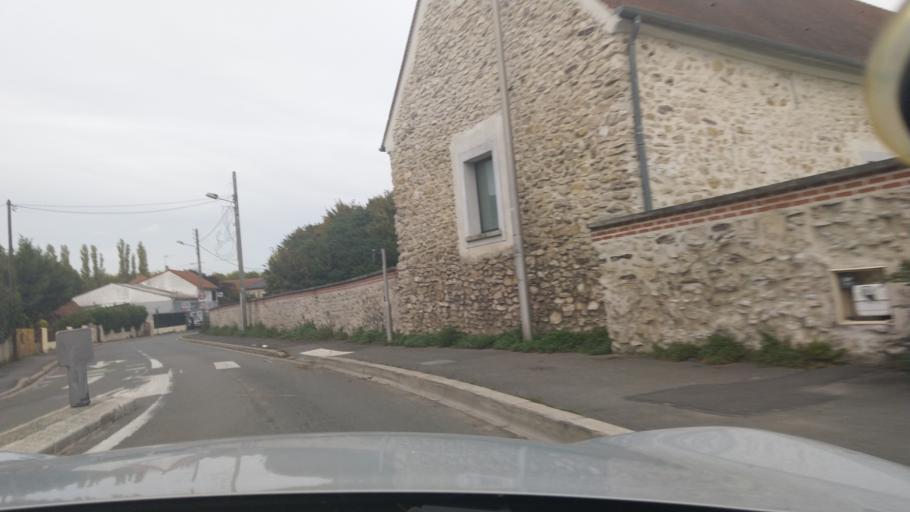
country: FR
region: Ile-de-France
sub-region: Departement de Seine-Saint-Denis
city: Villepinte
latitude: 48.9829
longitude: 2.5519
